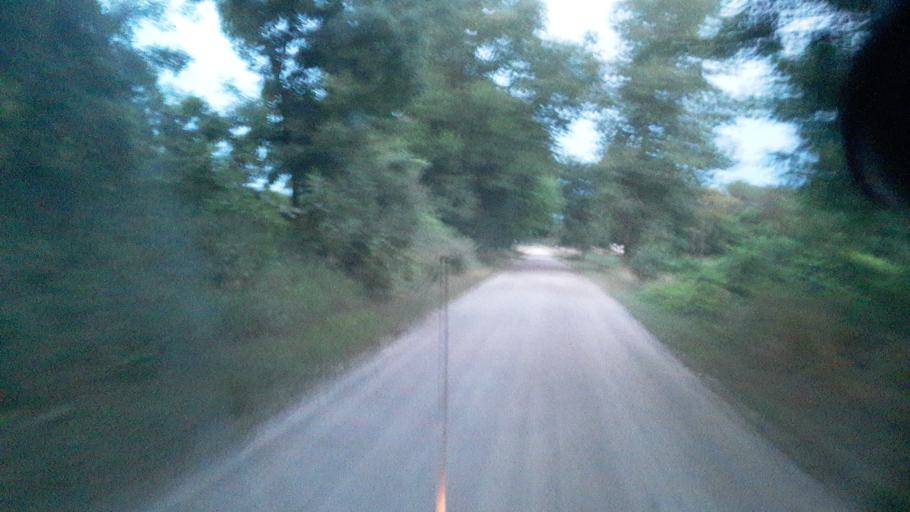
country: US
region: Indiana
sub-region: DeKalb County
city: Butler
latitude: 41.3608
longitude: -84.8255
